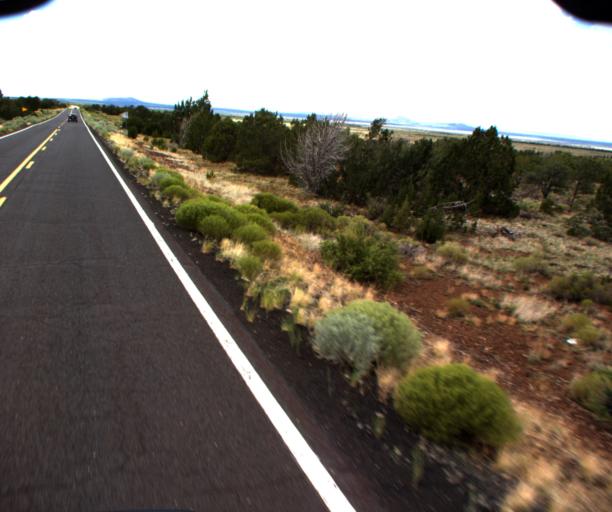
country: US
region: Arizona
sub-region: Coconino County
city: Parks
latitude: 35.5552
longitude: -111.8709
